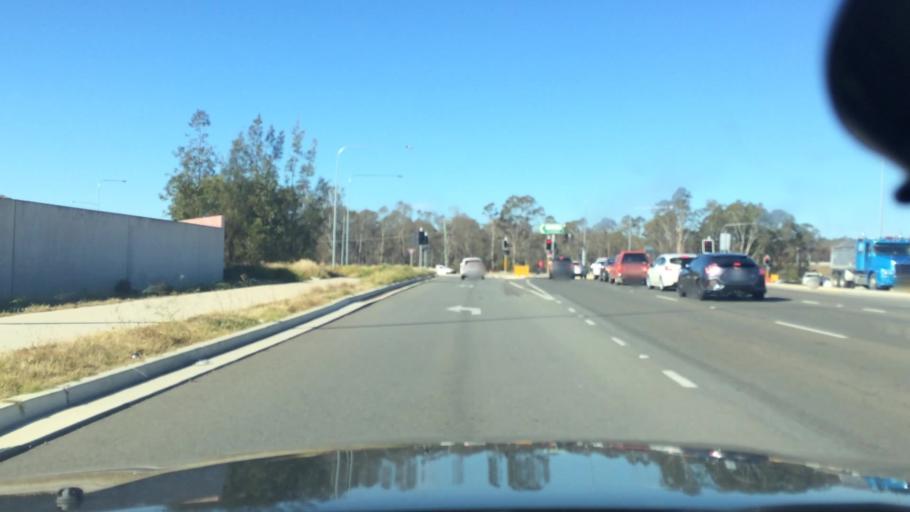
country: AU
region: New South Wales
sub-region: Campbelltown Municipality
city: Denham Court
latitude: -33.9489
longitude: 150.8387
